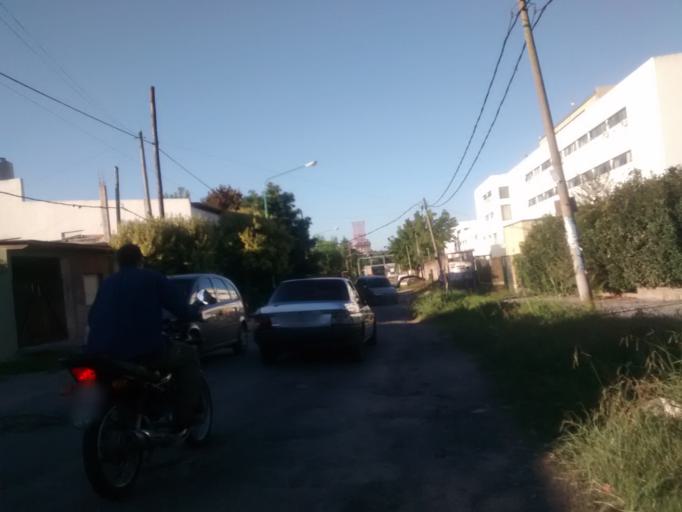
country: AR
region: Buenos Aires
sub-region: Partido de La Plata
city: La Plata
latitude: -34.9014
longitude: -57.9339
